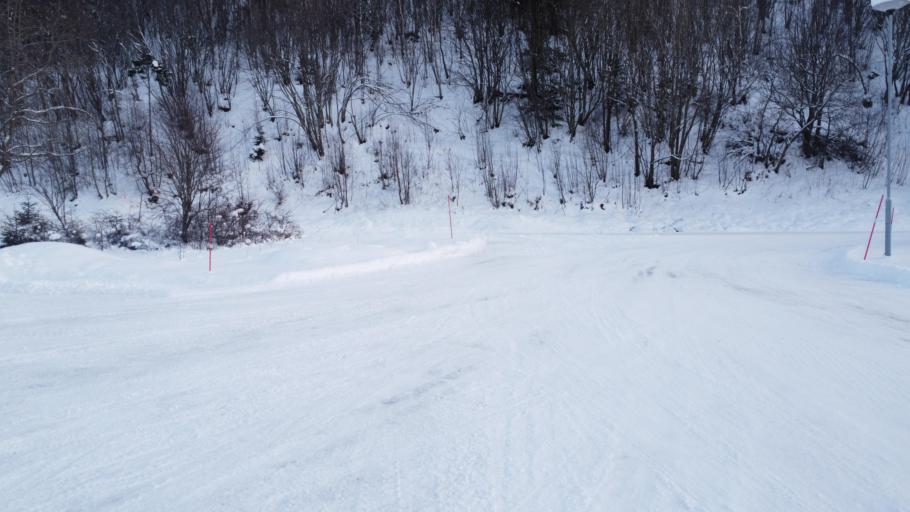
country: NO
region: Nordland
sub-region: Rana
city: Mo i Rana
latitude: 66.3225
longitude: 14.1539
